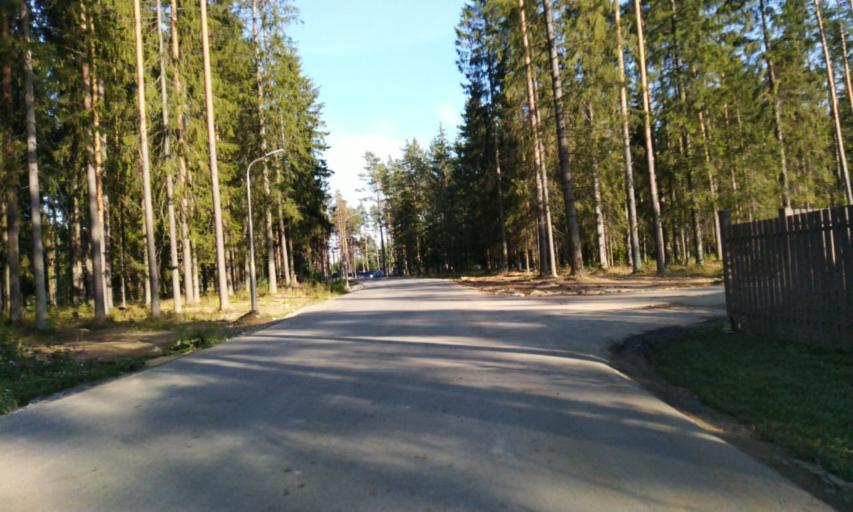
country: RU
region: Leningrad
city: Toksovo
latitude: 60.1288
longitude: 30.4601
